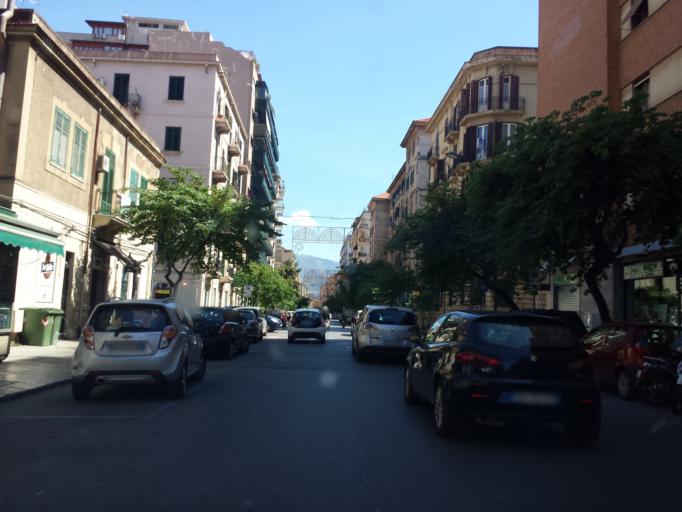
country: IT
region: Sicily
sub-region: Palermo
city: Palermo
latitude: 38.1316
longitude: 13.3437
